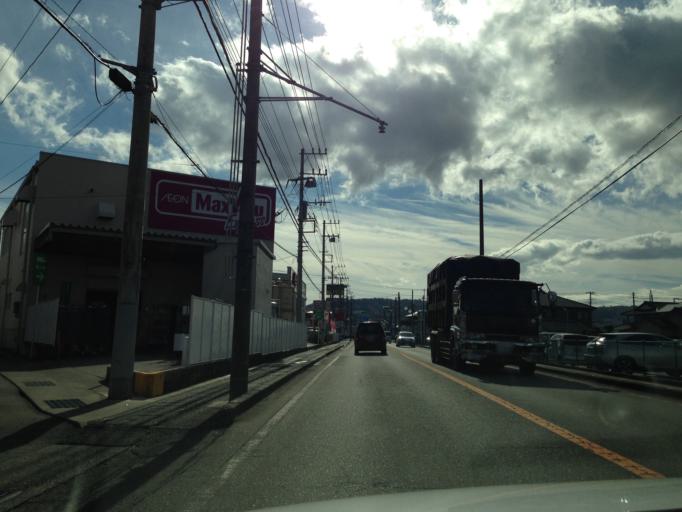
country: JP
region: Shizuoka
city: Mishima
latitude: 35.0144
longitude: 138.9442
